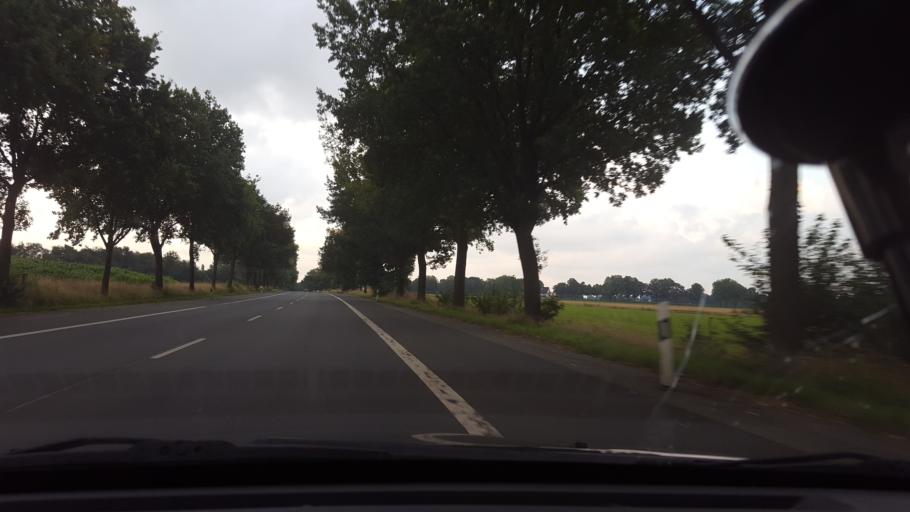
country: DE
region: North Rhine-Westphalia
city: Herten
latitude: 51.6310
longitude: 7.1473
